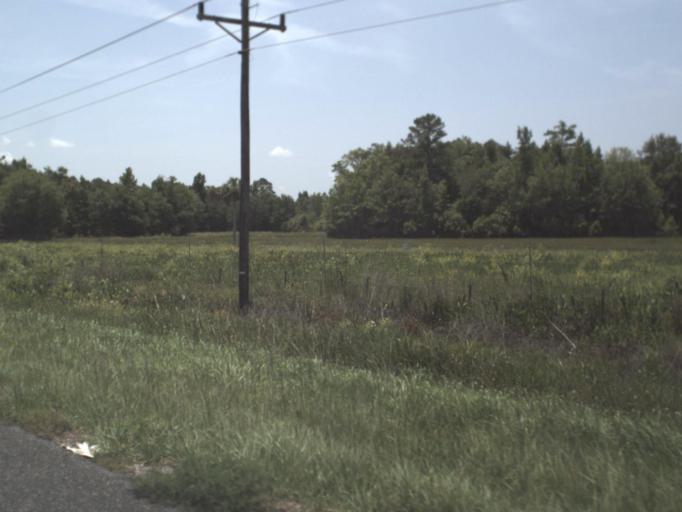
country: US
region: Florida
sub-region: Taylor County
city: Steinhatchee
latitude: 29.8411
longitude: -83.3713
